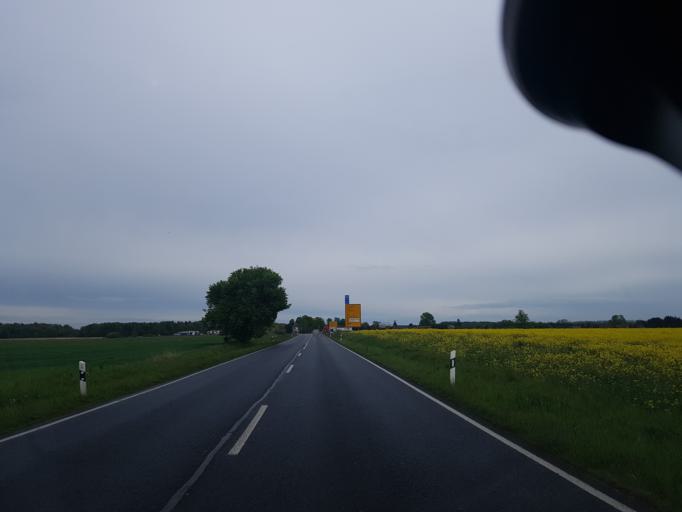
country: DE
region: Brandenburg
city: Grossraschen
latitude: 51.5861
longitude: 13.9496
